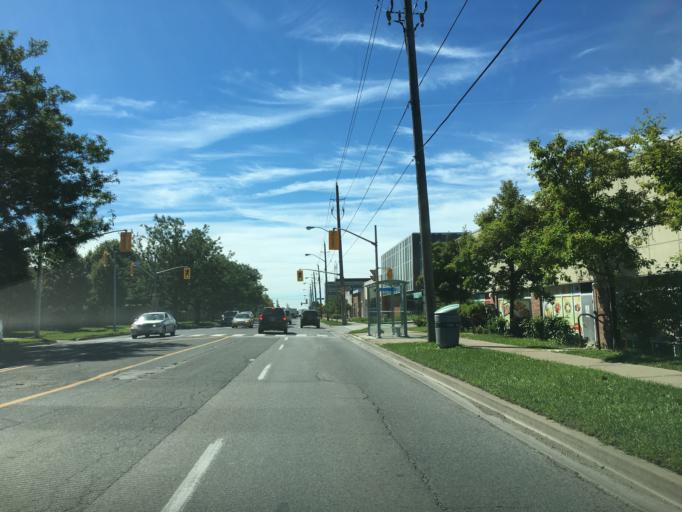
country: CA
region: Ontario
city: Markham
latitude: 43.8165
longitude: -79.2931
